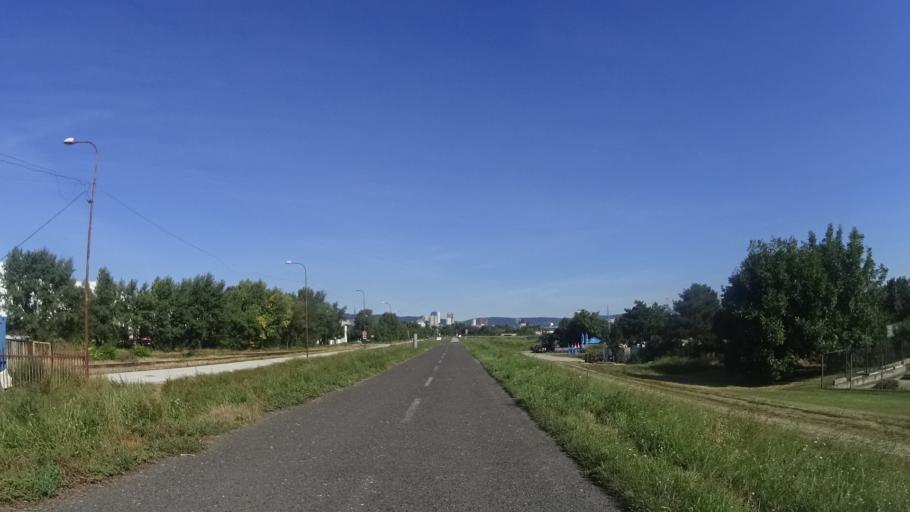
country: SK
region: Bratislavsky
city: Bratislava
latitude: 48.1325
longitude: 17.1558
